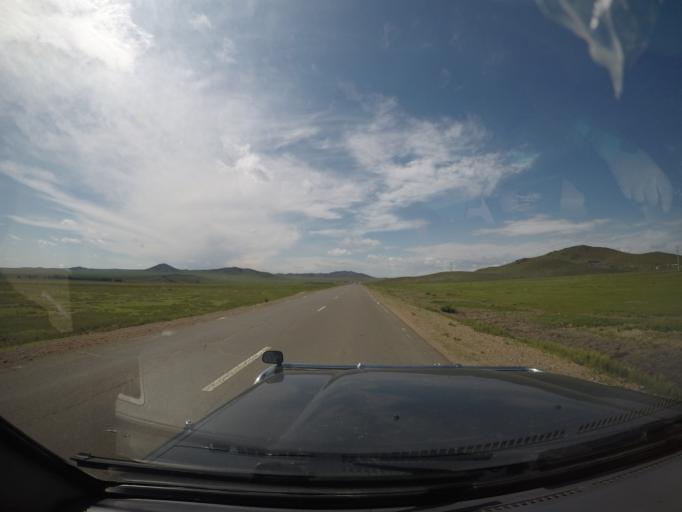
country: MN
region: Hentiy
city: Moron
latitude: 47.3807
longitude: 110.3612
